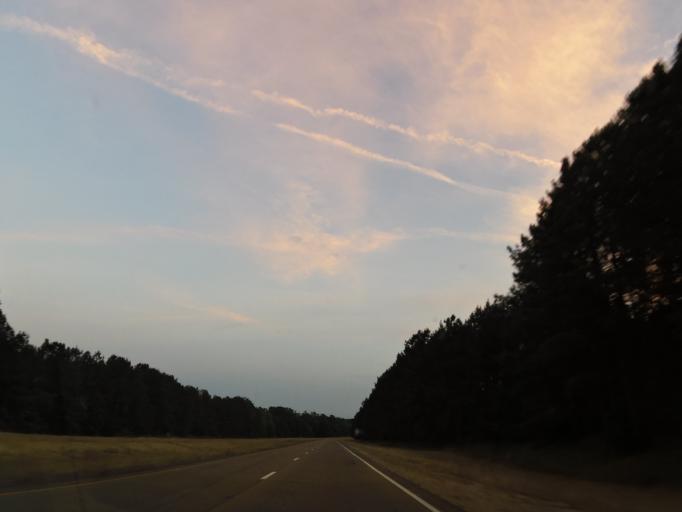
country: US
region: Mississippi
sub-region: Lauderdale County
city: Meridian Station
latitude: 32.6077
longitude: -88.4989
